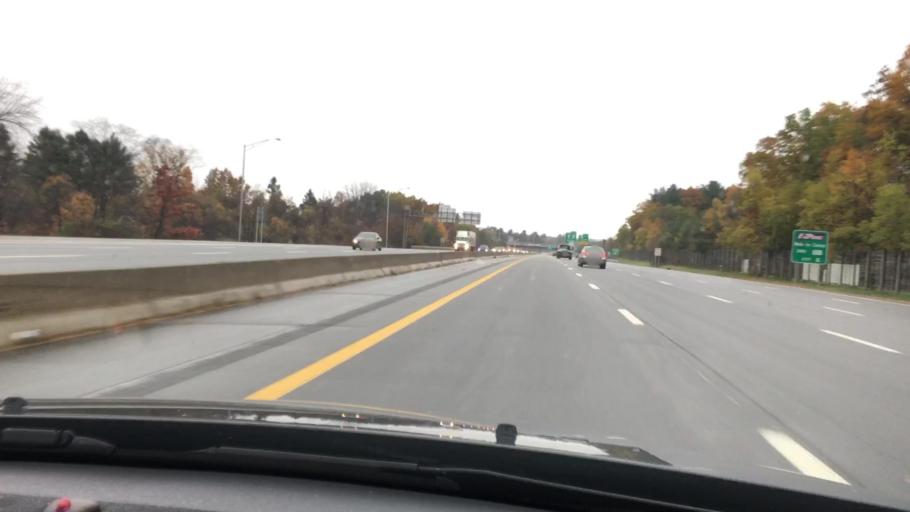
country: US
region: New Hampshire
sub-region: Hillsborough County
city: Nashua
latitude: 42.7850
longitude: -71.4948
